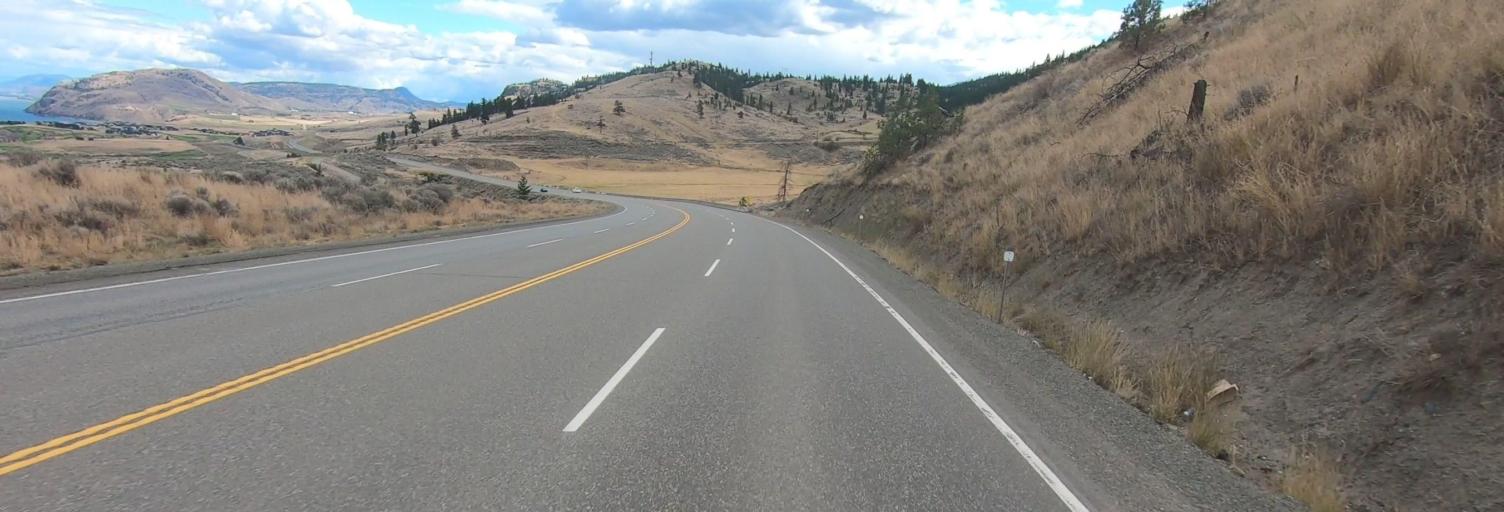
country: CA
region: British Columbia
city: Logan Lake
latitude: 50.7486
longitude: -120.7185
